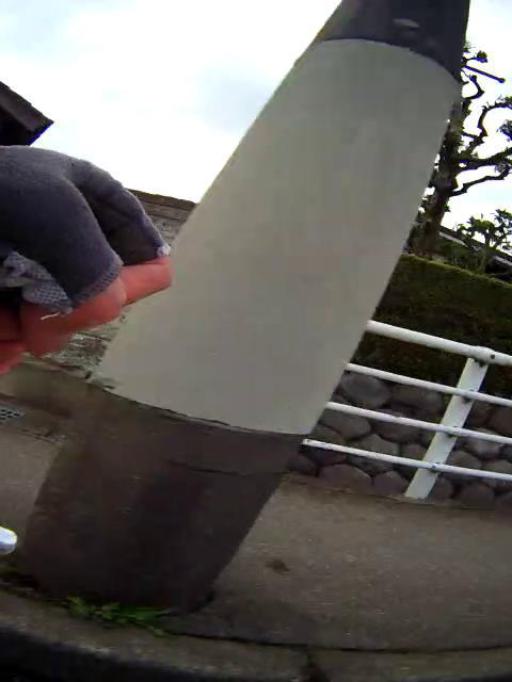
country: JP
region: Toyama
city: Takaoka
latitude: 36.7208
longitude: 136.9935
